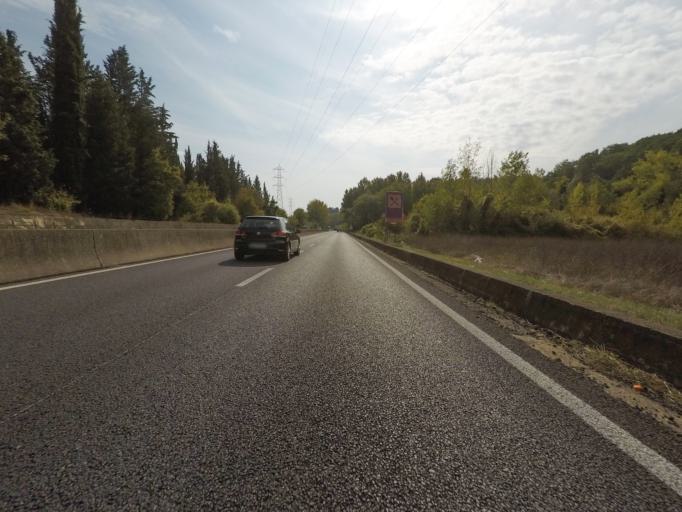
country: IT
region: Tuscany
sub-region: Provincia di Siena
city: Siena
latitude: 43.3217
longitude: 11.2992
